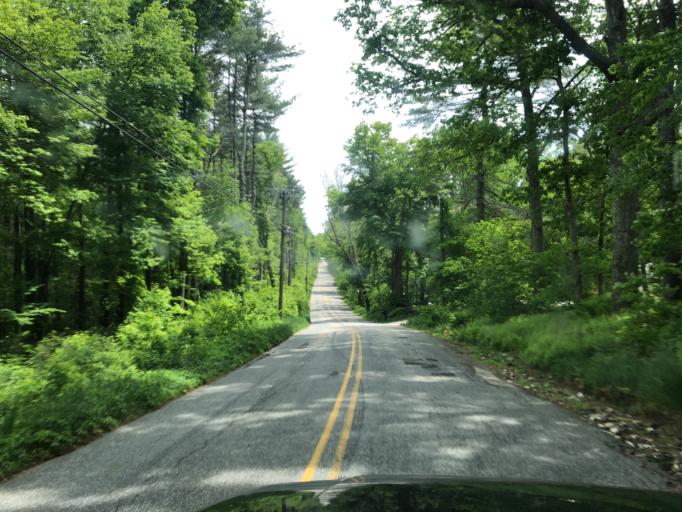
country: US
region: Connecticut
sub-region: Windham County
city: Thompson
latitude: 41.9652
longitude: -71.8301
